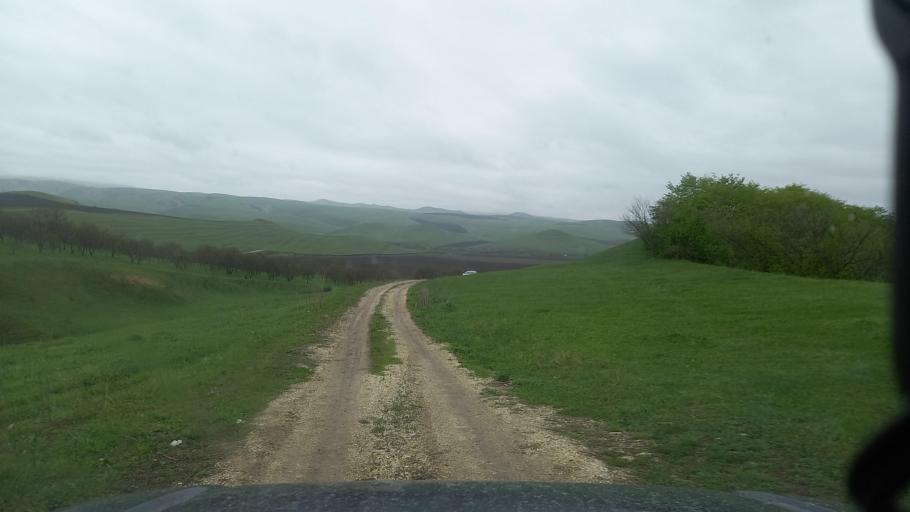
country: RU
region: Kabardino-Balkariya
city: Kamennomostskoye
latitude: 43.7074
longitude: 43.0745
